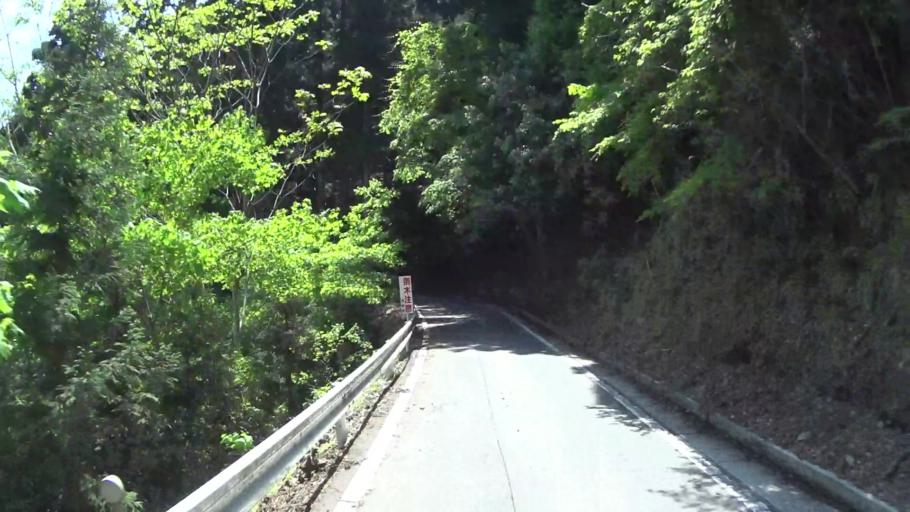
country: JP
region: Kyoto
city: Kameoka
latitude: 35.1290
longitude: 135.5792
